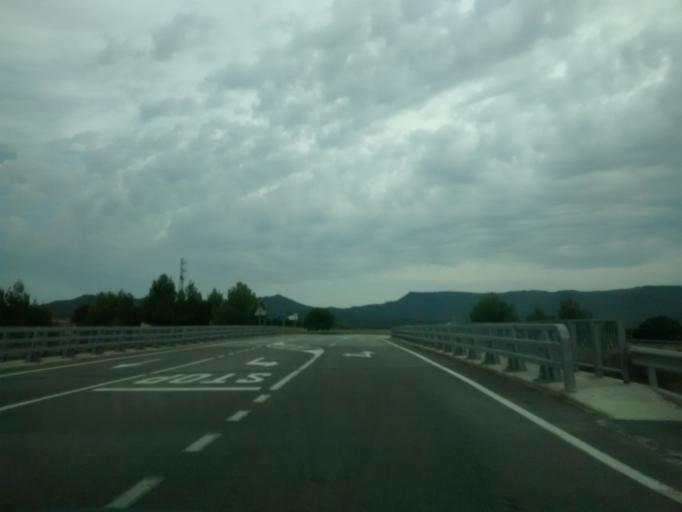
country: ES
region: Catalonia
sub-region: Provincia de Barcelona
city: Rajadell
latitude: 41.7391
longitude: 1.7094
